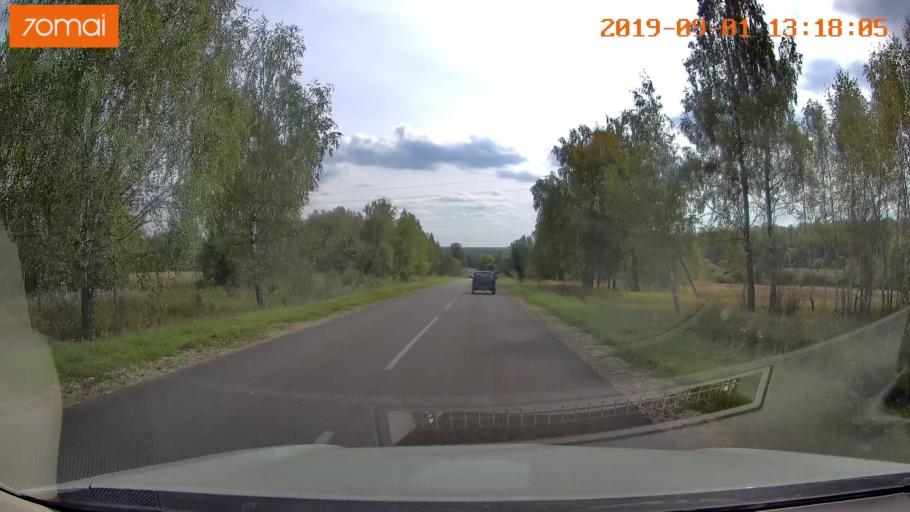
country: RU
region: Kaluga
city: Maloyaroslavets
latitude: 54.9285
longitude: 36.4721
